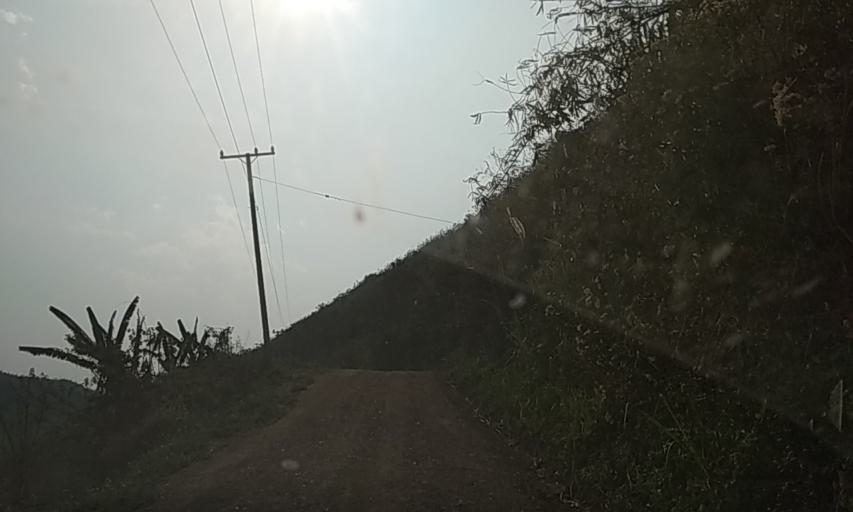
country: LA
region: Louangphabang
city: Louangphabang
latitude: 20.0478
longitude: 101.8469
